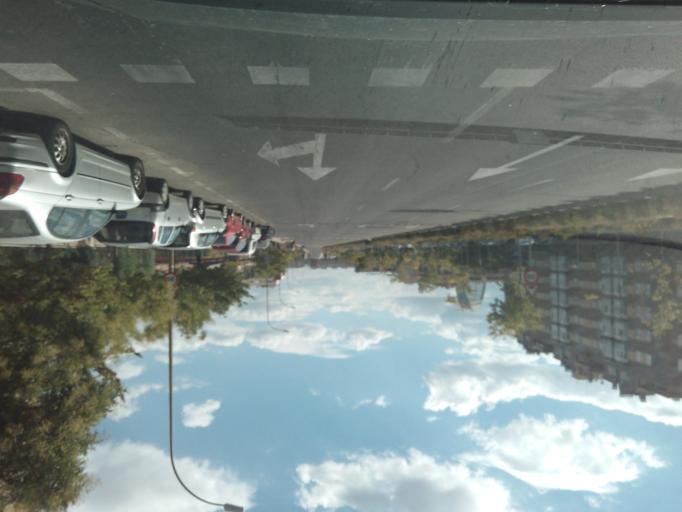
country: ES
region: Madrid
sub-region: Provincia de Madrid
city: Las Tablas
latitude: 40.4978
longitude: -3.6543
